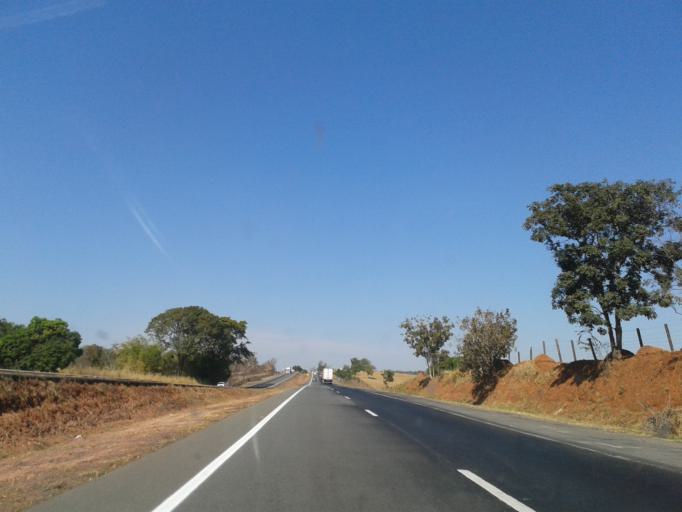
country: BR
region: Goias
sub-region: Piracanjuba
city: Piracanjuba
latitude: -17.3099
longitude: -49.2375
